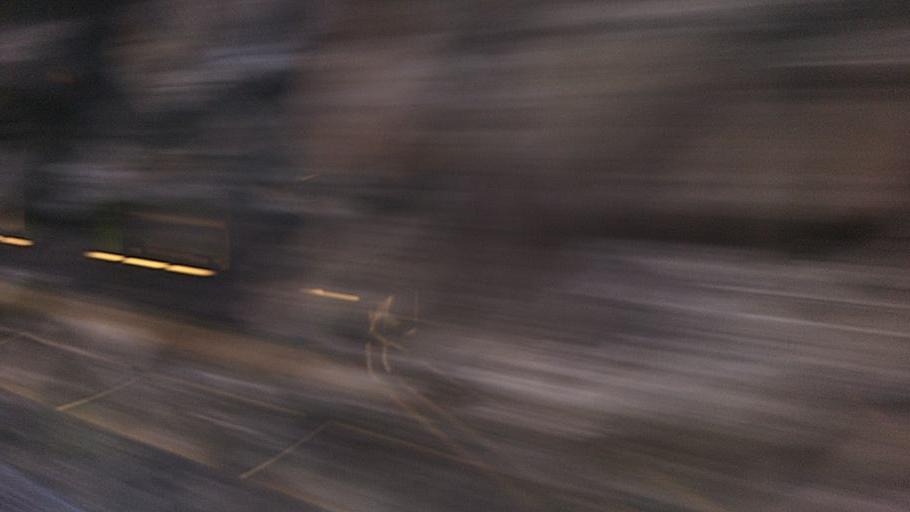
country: PT
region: Guarda
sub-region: Fornos de Algodres
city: Fornos de Algodres
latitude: 40.6016
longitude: -7.5505
